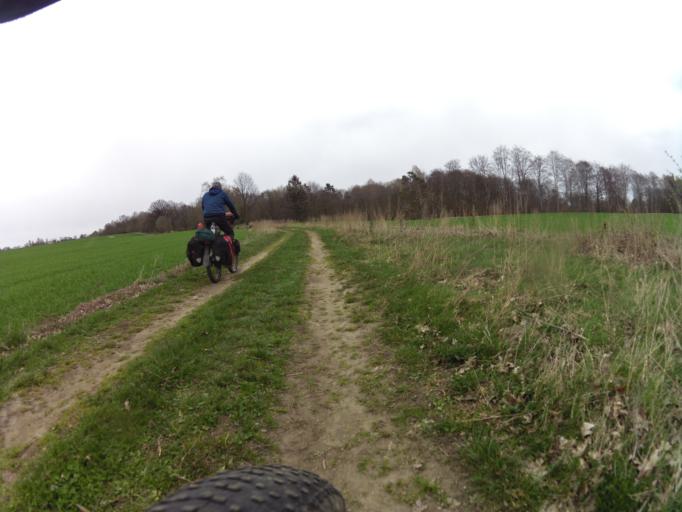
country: PL
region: West Pomeranian Voivodeship
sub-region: Powiat koszalinski
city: Polanow
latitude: 54.1215
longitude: 16.6185
